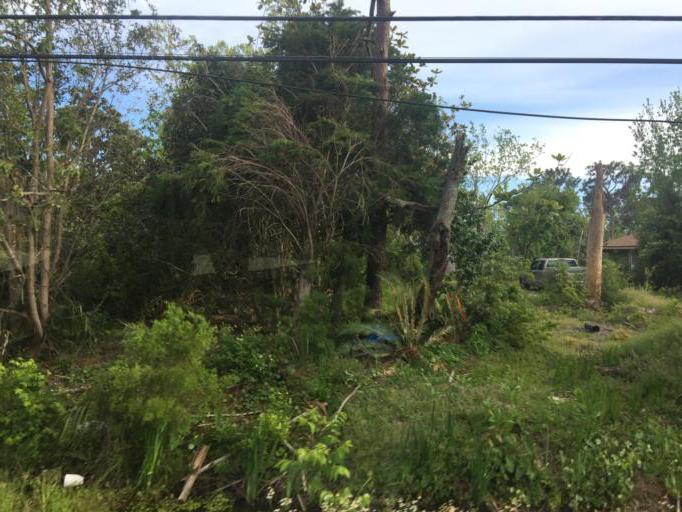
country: US
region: Florida
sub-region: Bay County
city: Panama City Beach
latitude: 30.1786
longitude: -85.7739
